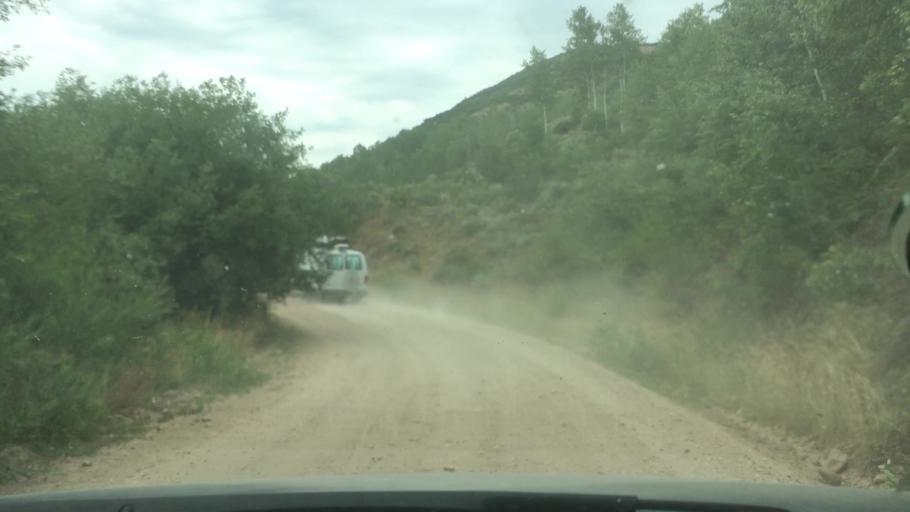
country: US
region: Utah
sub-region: Summit County
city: Summit Park
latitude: 40.8144
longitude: -111.5856
